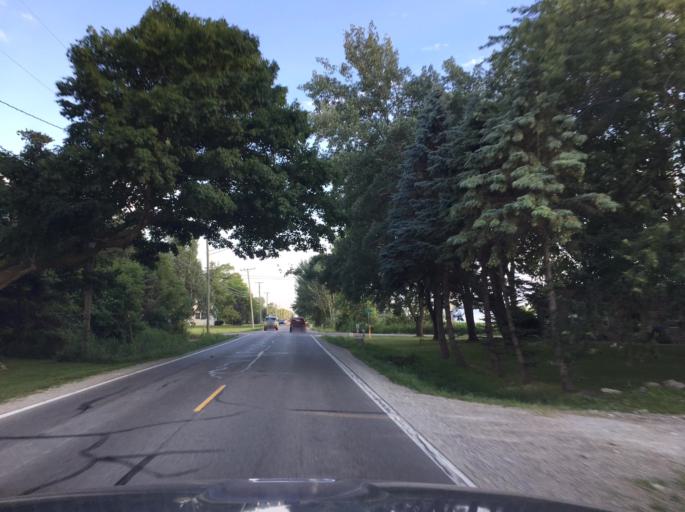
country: US
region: Michigan
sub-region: Macomb County
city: Romeo
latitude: 42.7463
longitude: -82.9605
